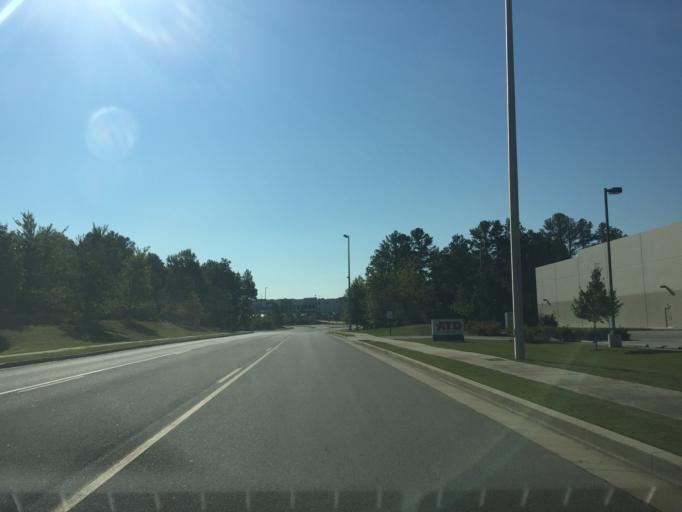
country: US
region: Tennessee
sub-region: Hamilton County
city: Harrison
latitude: 35.0723
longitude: -85.1446
